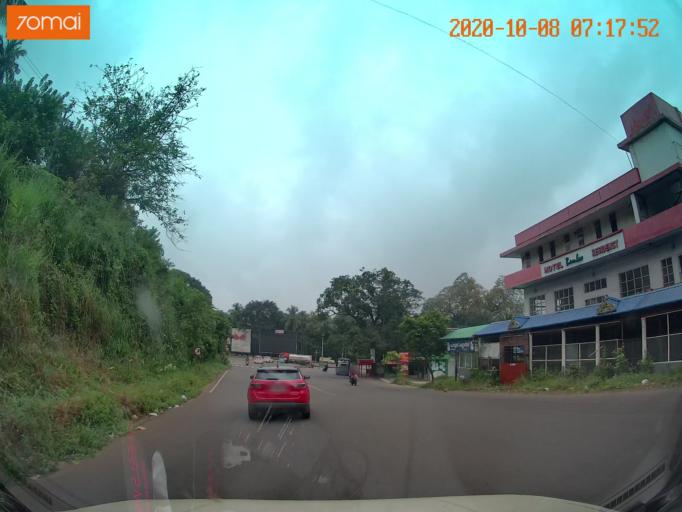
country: IN
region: Kerala
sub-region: Malappuram
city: Ponnani
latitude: 10.8396
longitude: 76.0216
